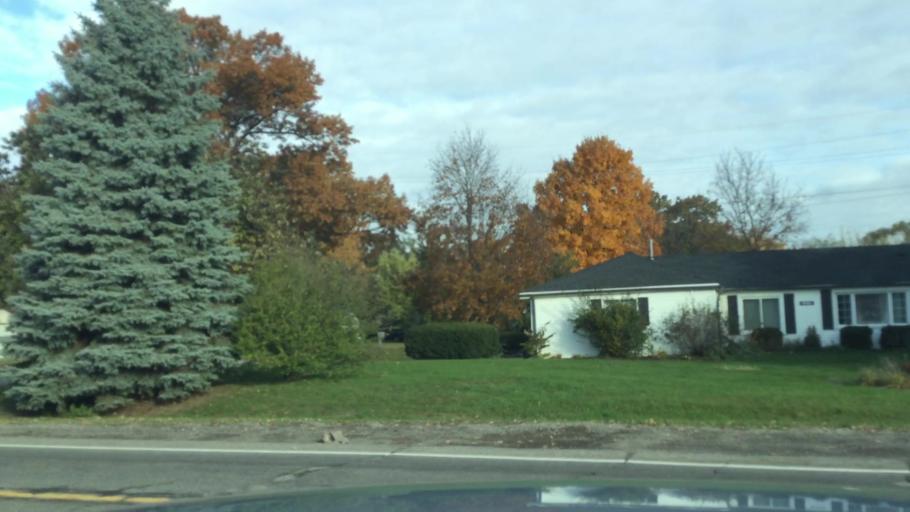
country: US
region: Michigan
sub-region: Wayne County
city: Westland
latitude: 42.3527
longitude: -83.4177
